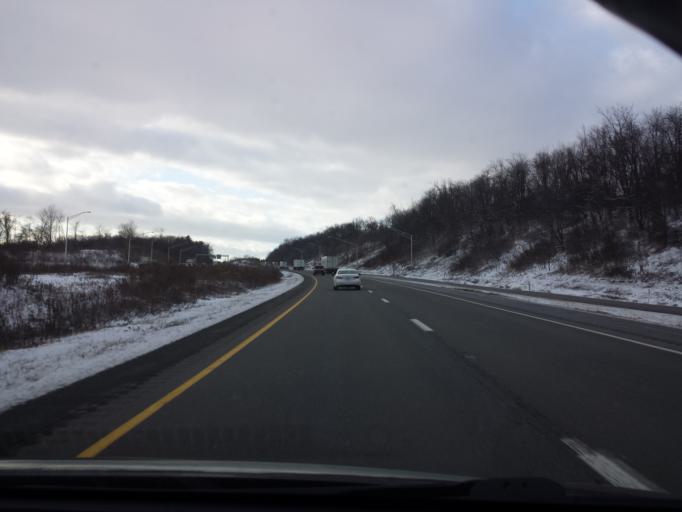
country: US
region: Pennsylvania
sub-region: Columbia County
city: Mifflinville
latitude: 41.0356
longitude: -76.3396
